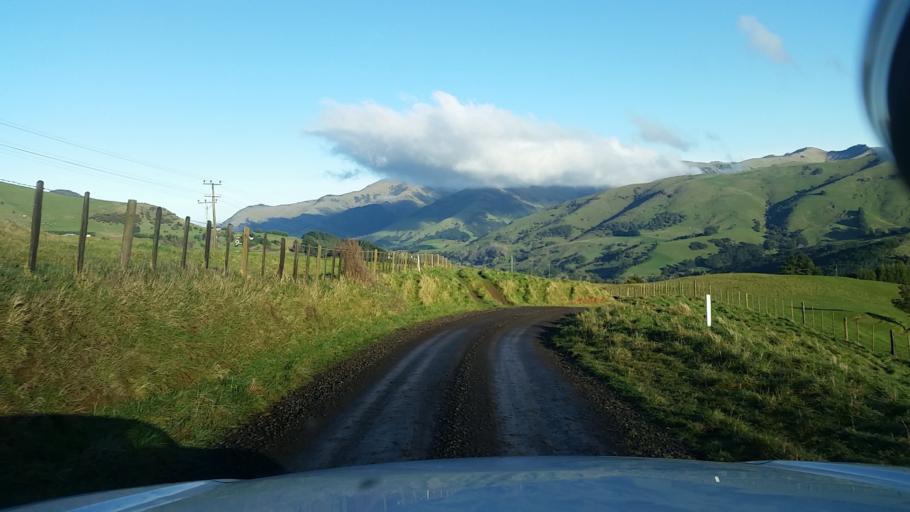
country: NZ
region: Canterbury
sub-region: Christchurch City
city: Christchurch
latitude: -43.7440
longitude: 172.8578
